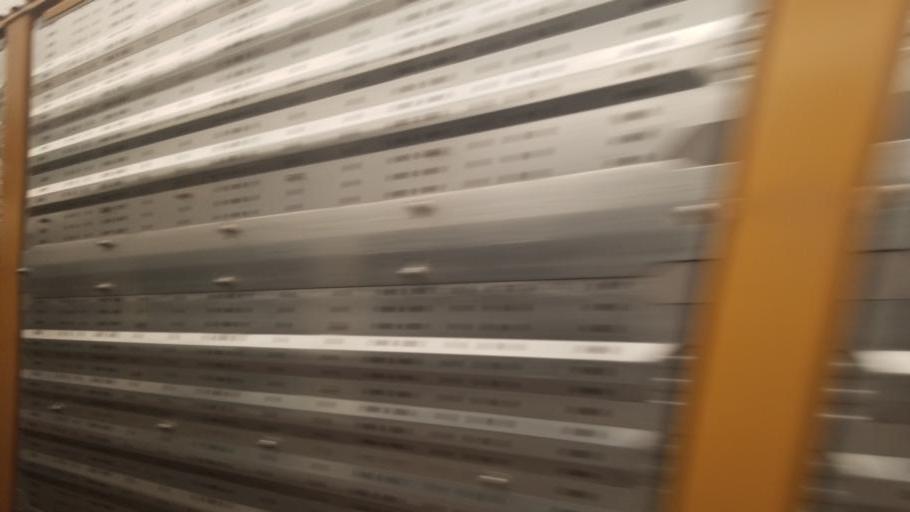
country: US
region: Pennsylvania
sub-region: Somerset County
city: Milford
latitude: 39.8809
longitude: -79.0927
